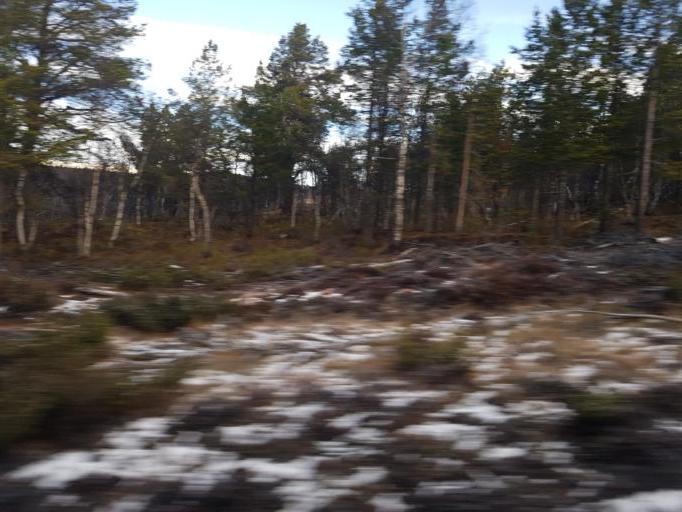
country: NO
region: Oppland
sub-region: Dovre
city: Dombas
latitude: 62.1076
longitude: 9.1981
